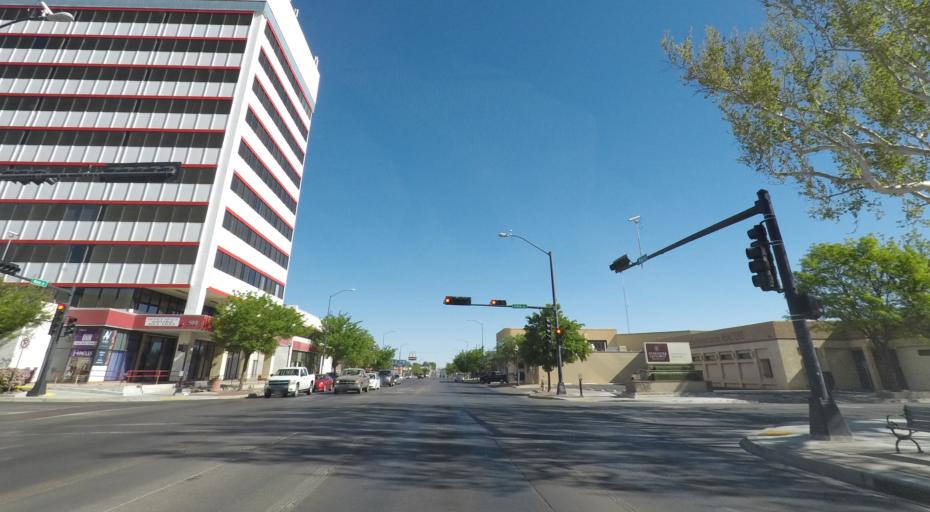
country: US
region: New Mexico
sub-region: Chaves County
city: Roswell
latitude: 33.3974
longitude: -104.5228
